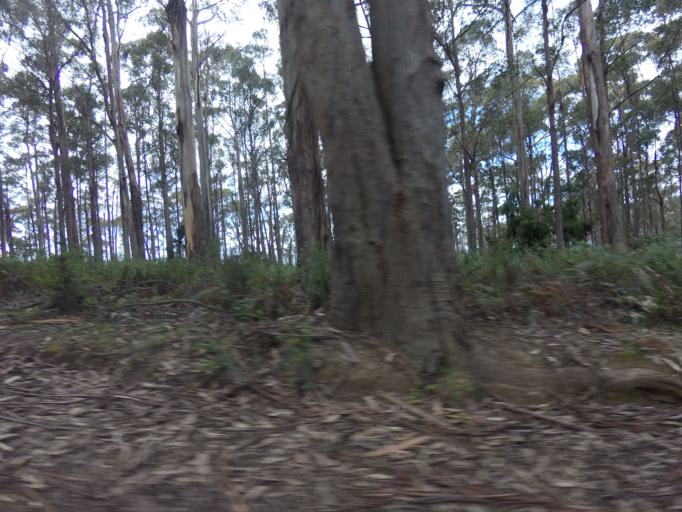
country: AU
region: Tasmania
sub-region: Huon Valley
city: Geeveston
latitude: -43.4156
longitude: 147.0161
